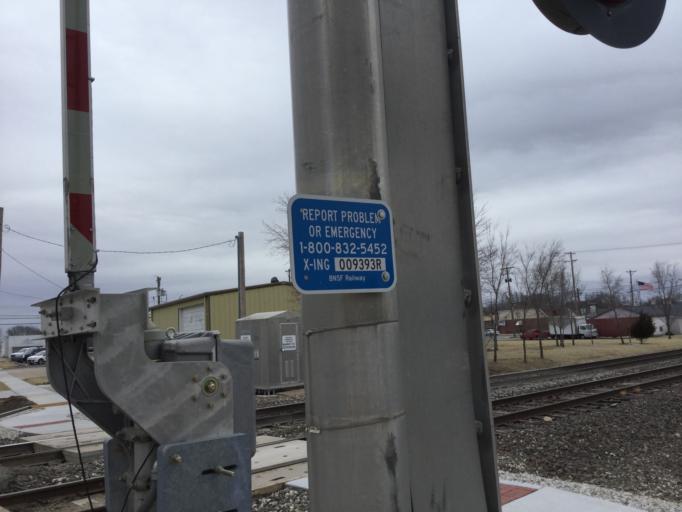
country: US
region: Kansas
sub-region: Sedgwick County
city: Derby
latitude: 37.5443
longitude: -97.2717
